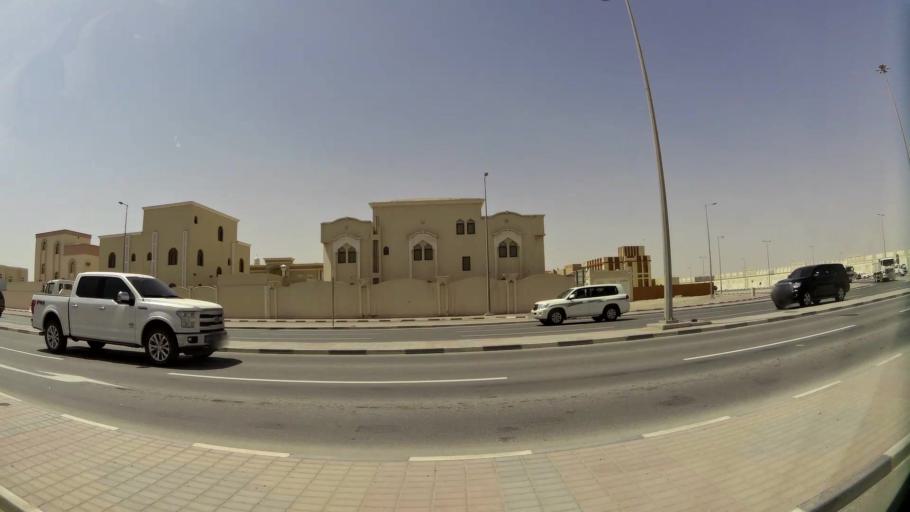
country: QA
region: Baladiyat Umm Salal
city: Umm Salal Muhammad
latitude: 25.3897
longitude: 51.4653
